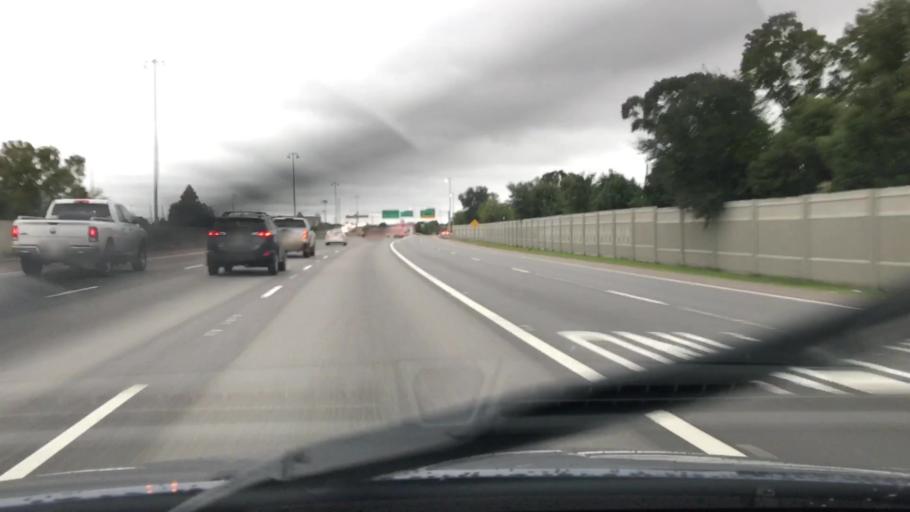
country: US
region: Louisiana
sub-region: Jefferson Parish
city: Kenner
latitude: 30.0024
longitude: -90.2031
